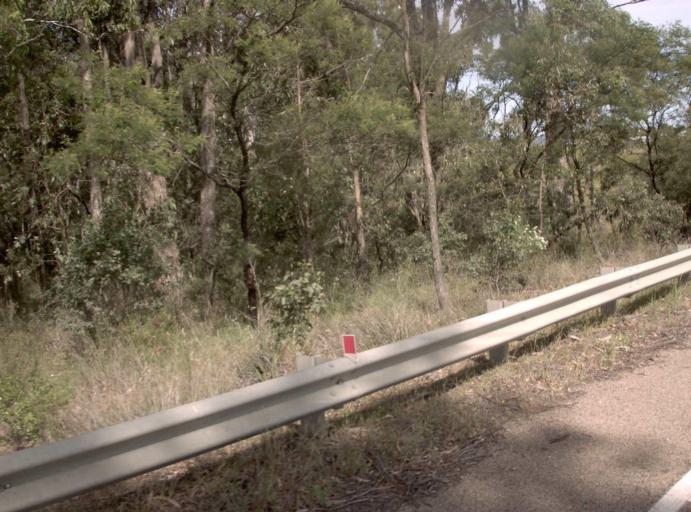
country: AU
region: Victoria
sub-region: East Gippsland
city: Lakes Entrance
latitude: -37.8413
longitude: 147.9283
